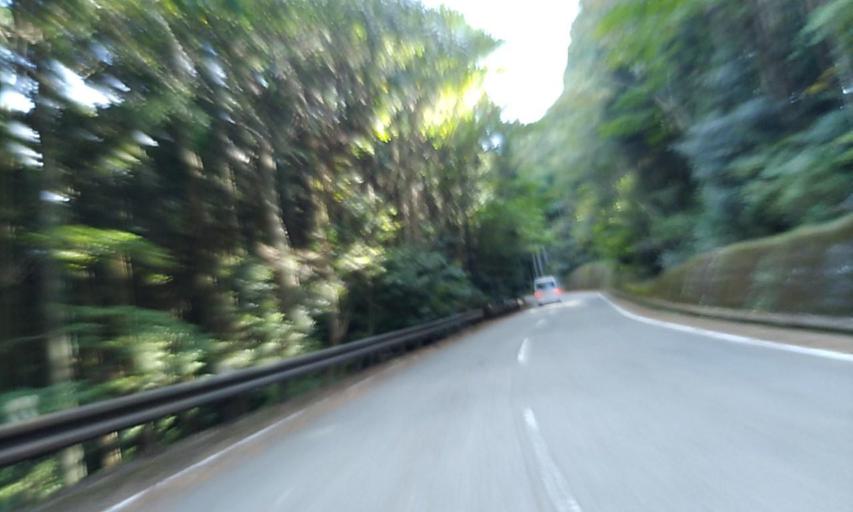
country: JP
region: Wakayama
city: Iwade
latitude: 34.1163
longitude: 135.3431
